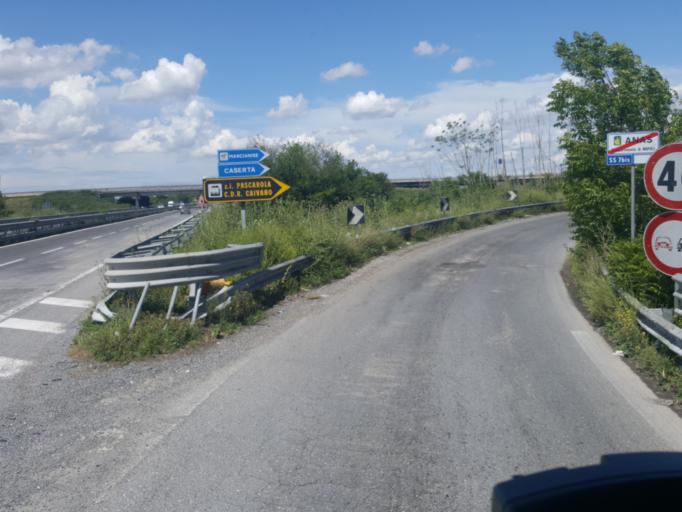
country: IT
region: Campania
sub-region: Provincia di Napoli
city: Pascarola
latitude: 40.9735
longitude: 14.2964
